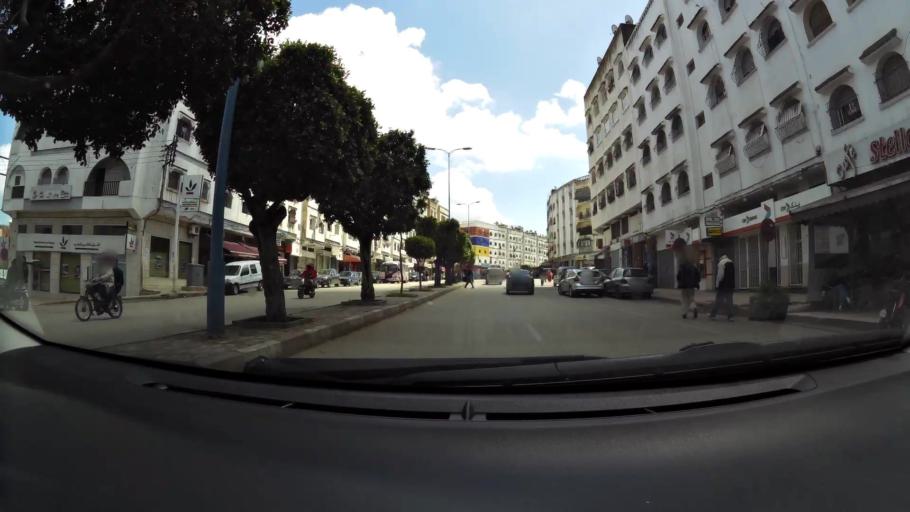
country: MA
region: Grand Casablanca
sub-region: Mediouna
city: Tit Mellil
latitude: 33.5381
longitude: -7.5529
